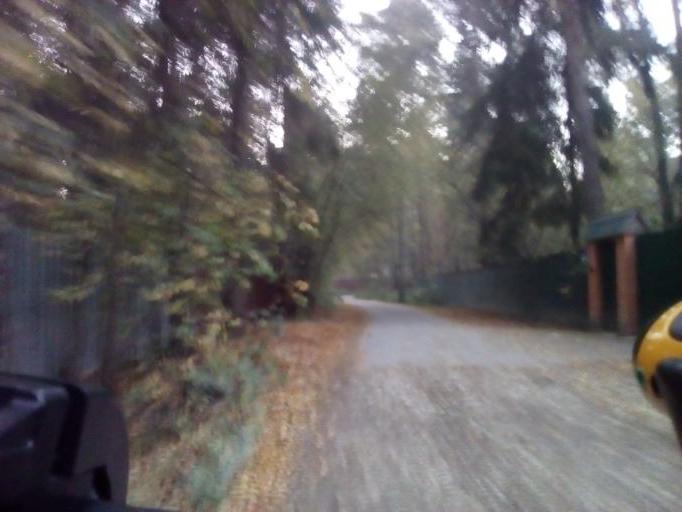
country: RU
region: Moskovskaya
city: Kratovo
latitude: 55.6040
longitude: 38.1758
